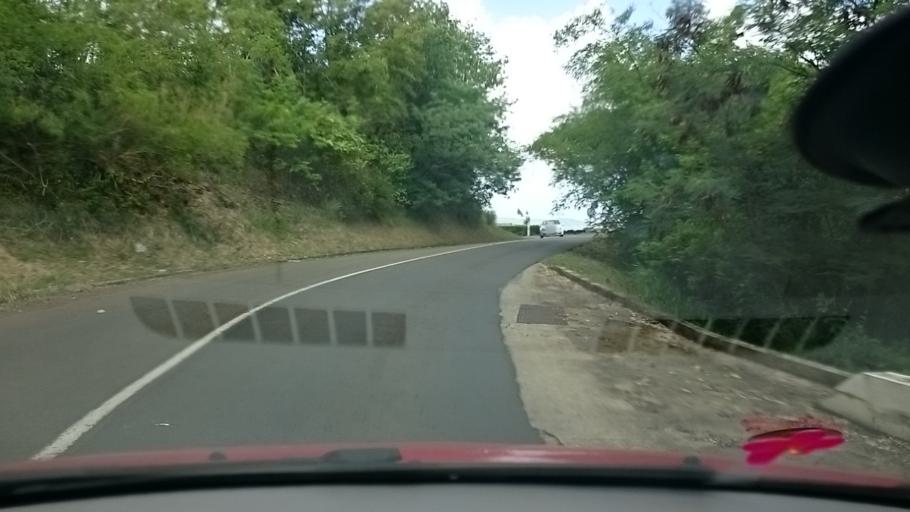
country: MQ
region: Martinique
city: Petite Riviere Salee
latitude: 14.7513
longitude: -60.9418
